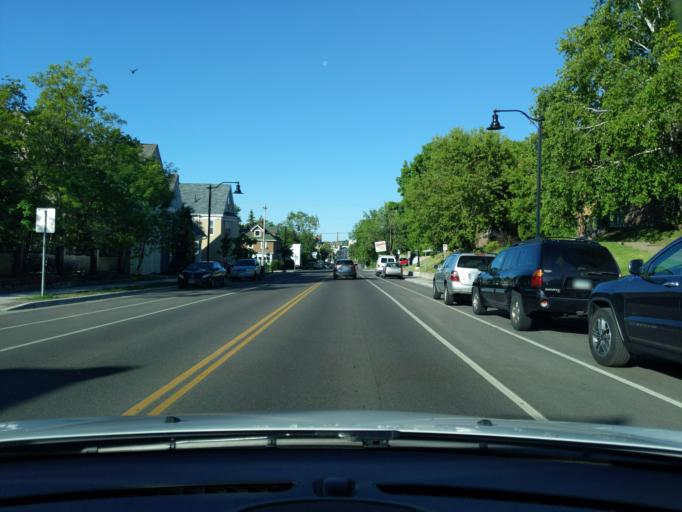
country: US
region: Minnesota
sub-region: Saint Louis County
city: Duluth
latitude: 46.8027
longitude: -92.0856
